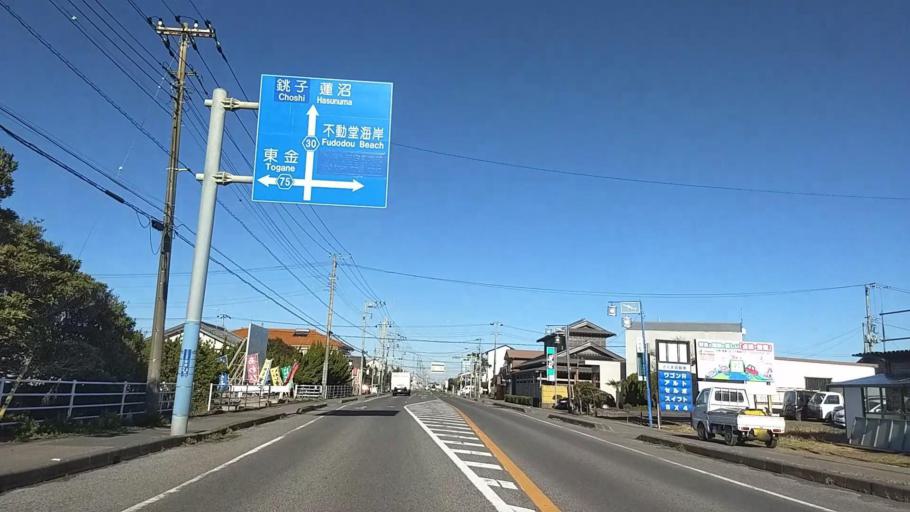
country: JP
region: Chiba
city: Togane
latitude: 35.5078
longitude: 140.4332
